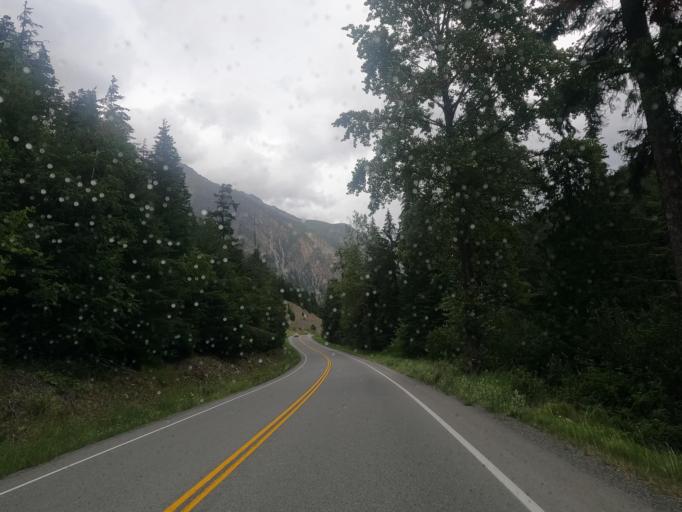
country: CA
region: British Columbia
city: Lillooet
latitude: 50.5220
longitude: -122.1648
